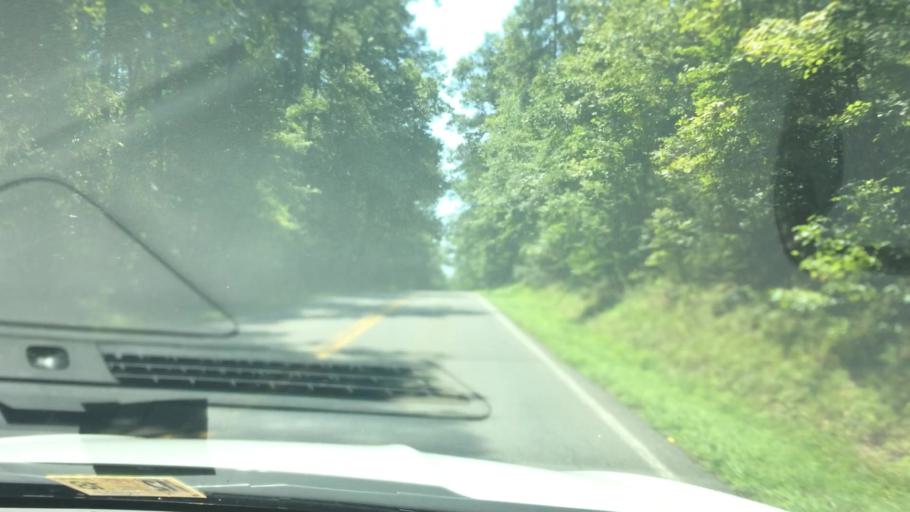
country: US
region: Virginia
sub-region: Charles City County
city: Charles City
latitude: 37.4040
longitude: -77.0472
